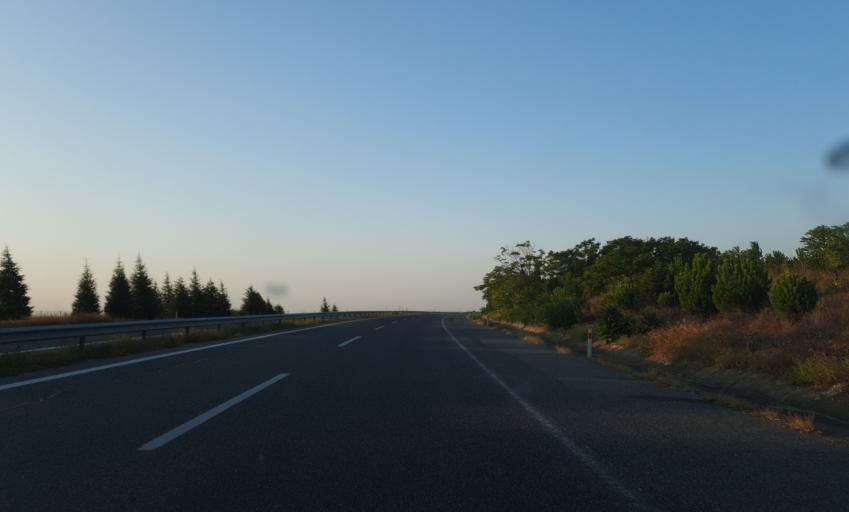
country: TR
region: Kirklareli
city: Luleburgaz
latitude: 41.4264
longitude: 27.3842
